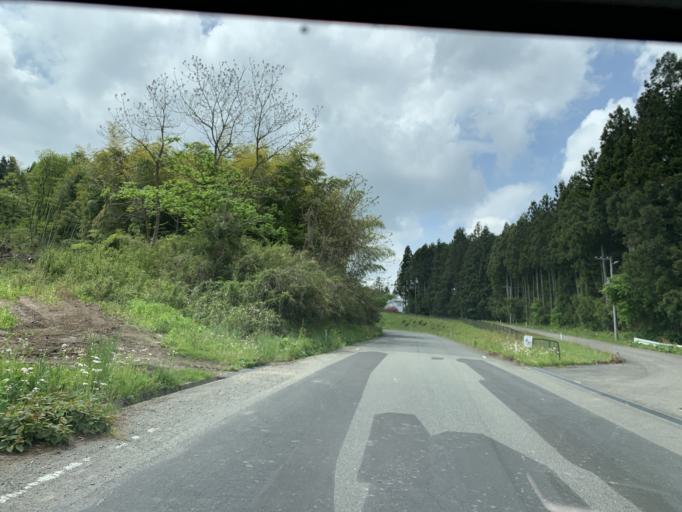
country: JP
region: Miyagi
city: Furukawa
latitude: 38.7303
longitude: 140.9273
